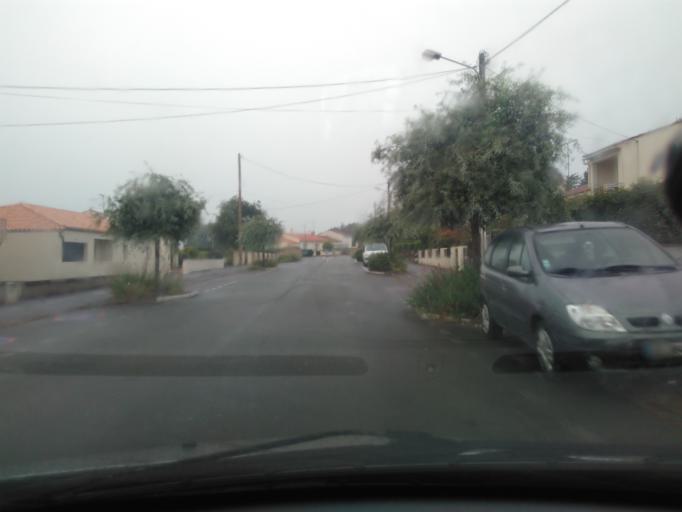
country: FR
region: Pays de la Loire
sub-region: Departement de la Vendee
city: Bretignolles-sur-Mer
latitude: 46.6254
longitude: -1.8590
